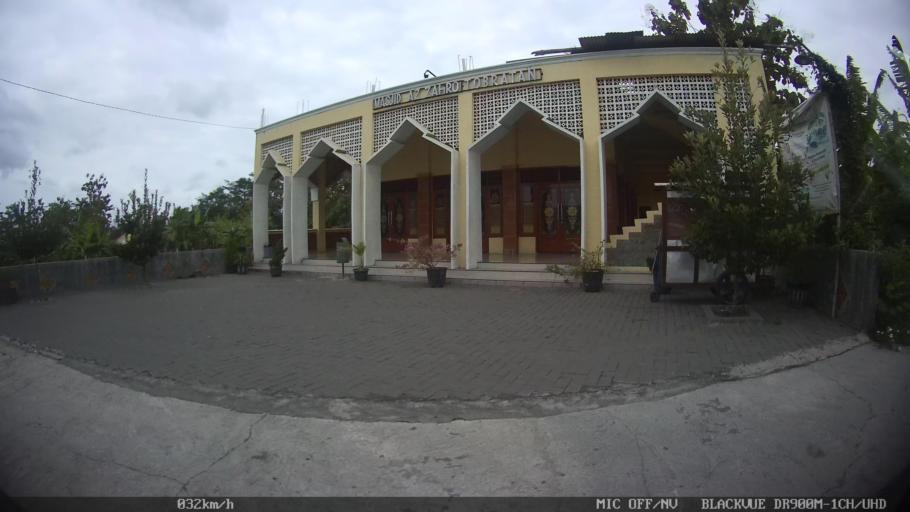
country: ID
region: Daerah Istimewa Yogyakarta
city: Sewon
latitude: -7.8616
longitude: 110.4014
